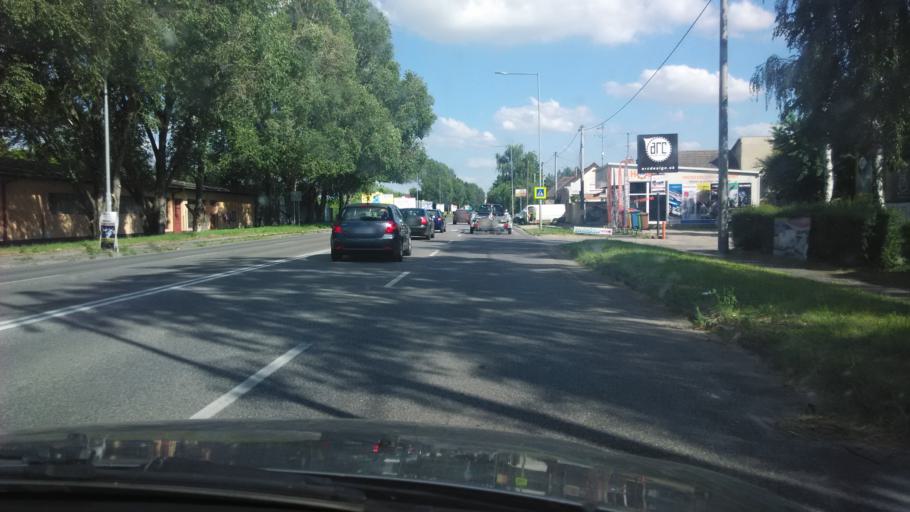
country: SK
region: Nitriansky
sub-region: Okres Nove Zamky
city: Nove Zamky
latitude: 48.0016
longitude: 18.1600
